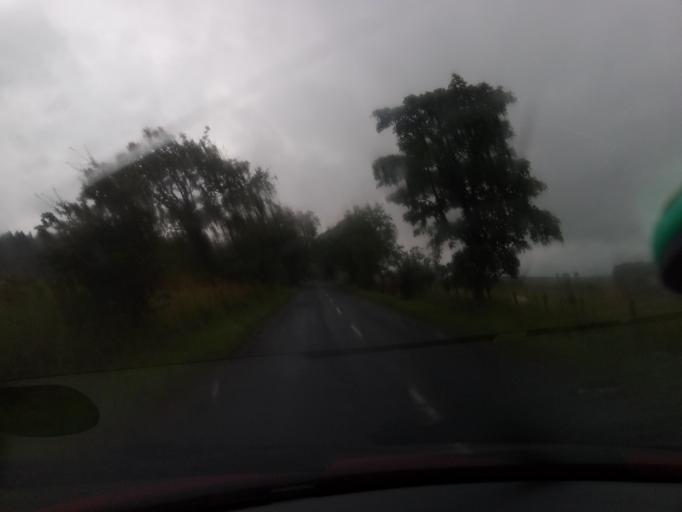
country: GB
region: England
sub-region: Northumberland
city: Rothley
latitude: 55.1714
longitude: -1.9893
